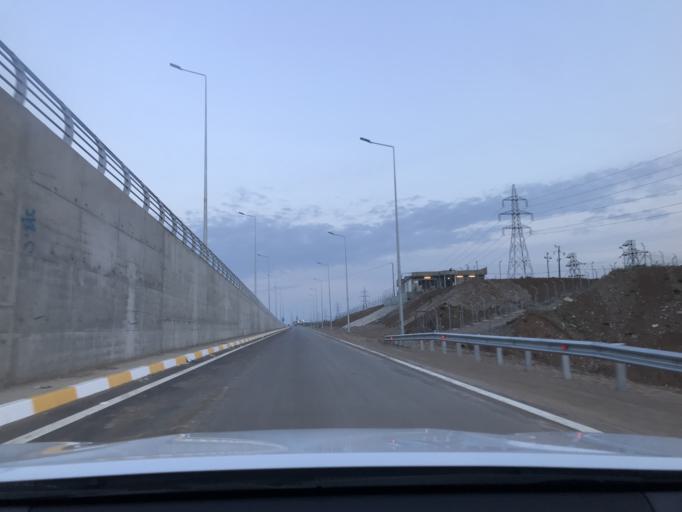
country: IQ
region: Arbil
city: Erbil
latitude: 36.3154
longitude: 43.9100
